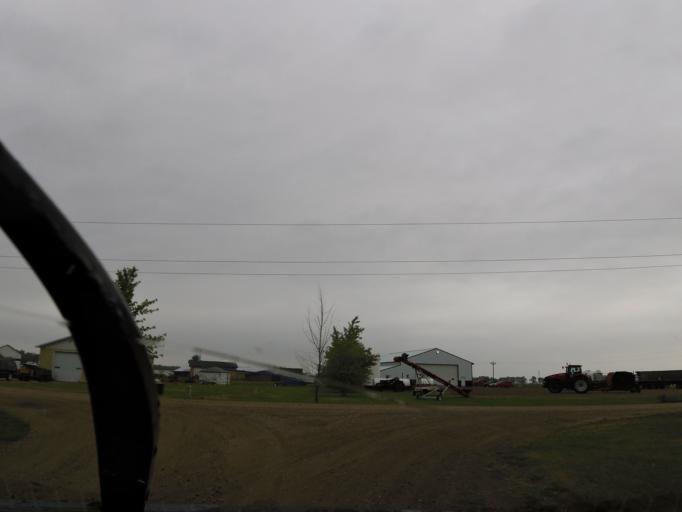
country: US
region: Minnesota
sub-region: Marshall County
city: Warren
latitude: 48.4537
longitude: -96.8705
